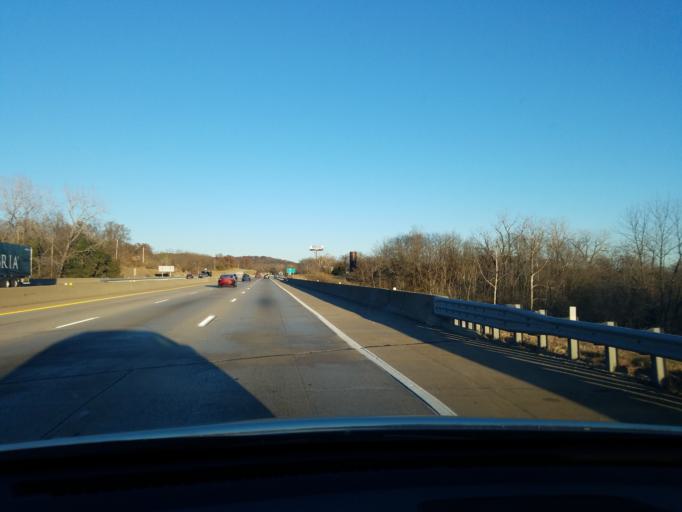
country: US
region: Missouri
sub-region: Franklin County
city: Gray Summit
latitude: 38.4862
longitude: -90.8113
